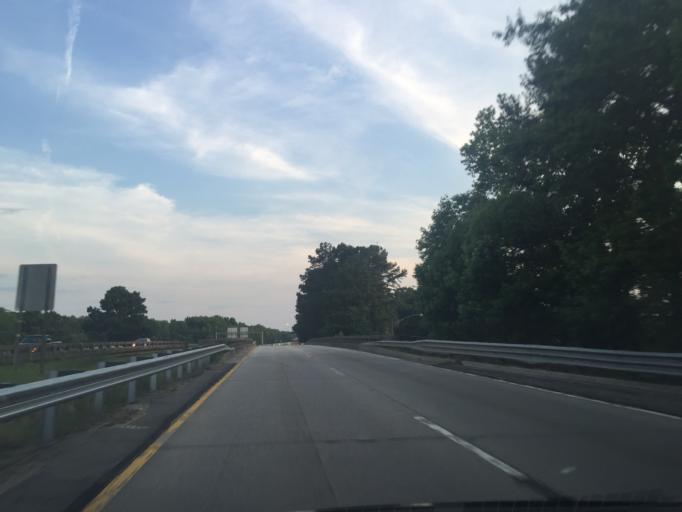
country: US
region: Georgia
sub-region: Chatham County
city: Savannah
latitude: 32.0544
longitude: -81.1415
